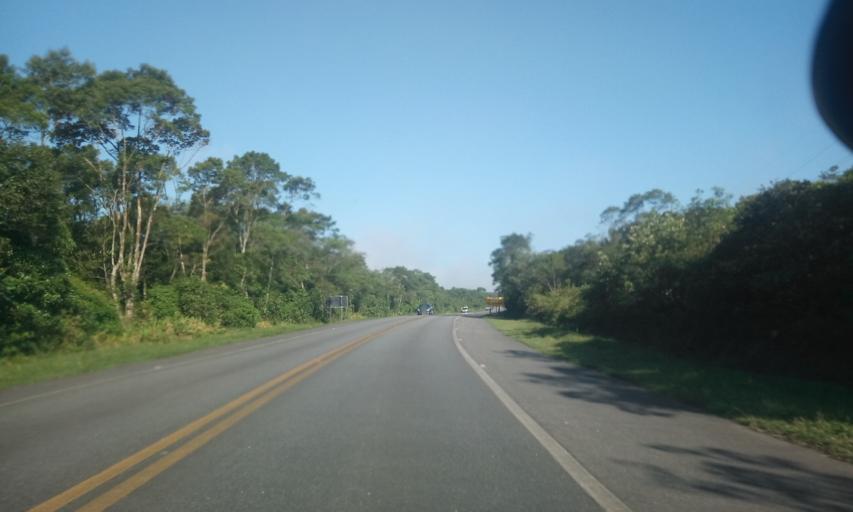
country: BR
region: Sao Paulo
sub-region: Cubatao
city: Cubatao
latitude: -23.8478
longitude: -46.4700
